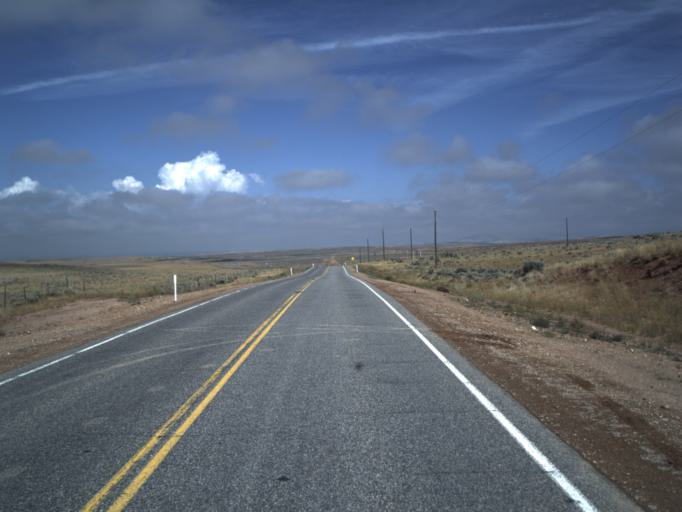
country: US
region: Wyoming
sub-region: Uinta County
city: Evanston
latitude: 41.4216
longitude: -111.0510
